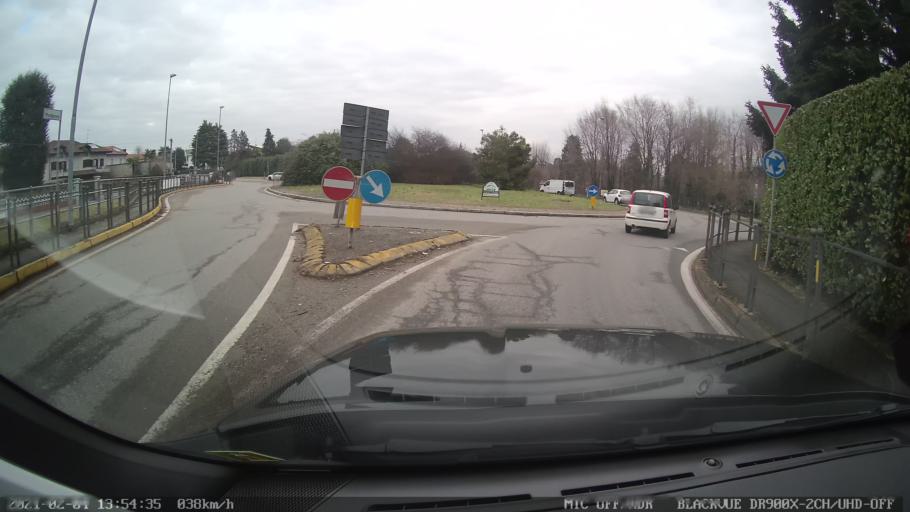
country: IT
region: Lombardy
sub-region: Provincia di Varese
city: Cairate
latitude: 45.6853
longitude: 8.8715
